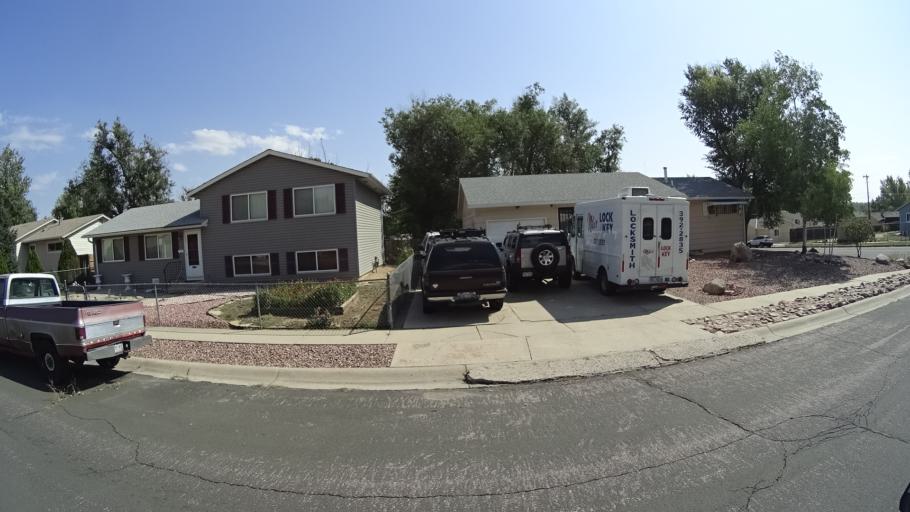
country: US
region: Colorado
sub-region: El Paso County
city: Colorado Springs
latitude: 38.8213
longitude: -104.7825
